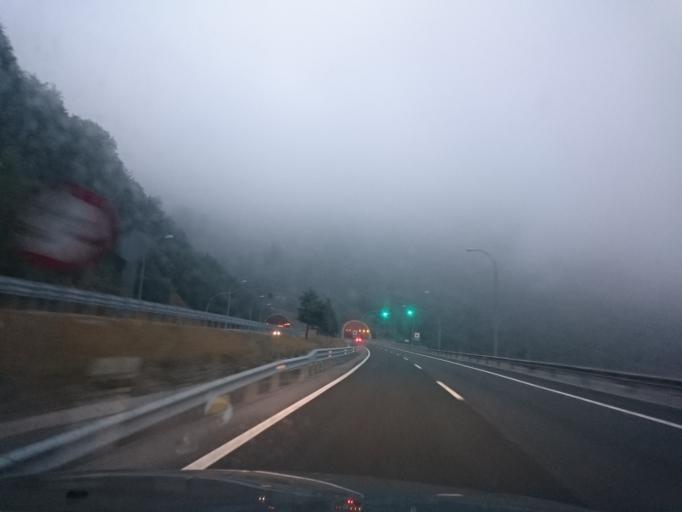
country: ES
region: Castille and Leon
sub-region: Provincia de Leon
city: Sena de Luna
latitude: 42.9927
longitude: -5.8160
